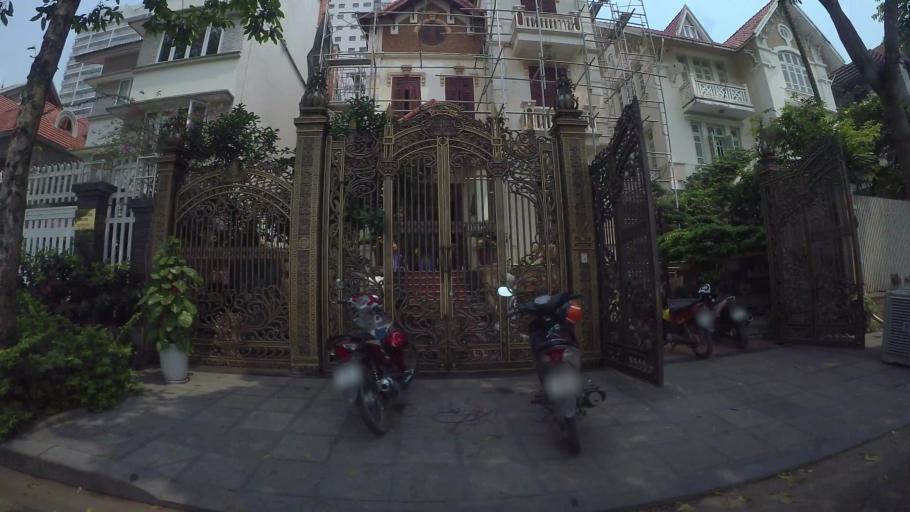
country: VN
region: Ha Noi
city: Van Dien
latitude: 20.9624
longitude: 105.8321
